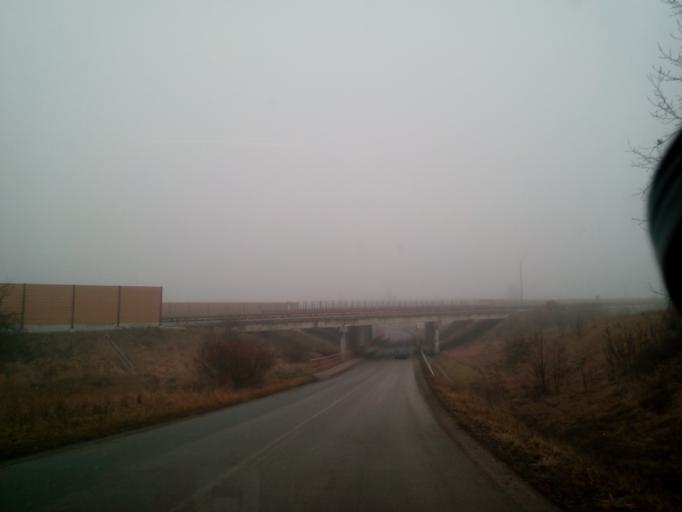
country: SK
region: Presovsky
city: Spisske Podhradie
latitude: 49.0069
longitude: 20.7631
